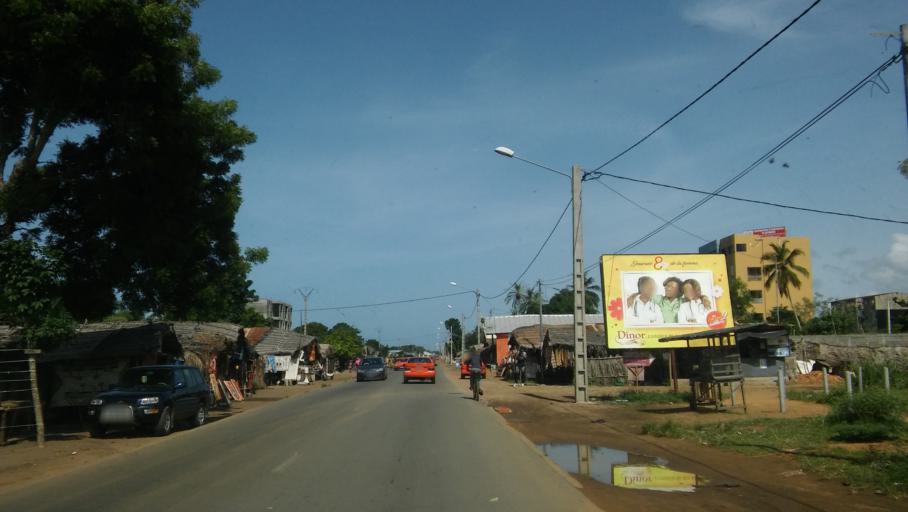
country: CI
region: Sud-Comoe
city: Grand-Bassam
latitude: 5.2103
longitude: -3.7578
